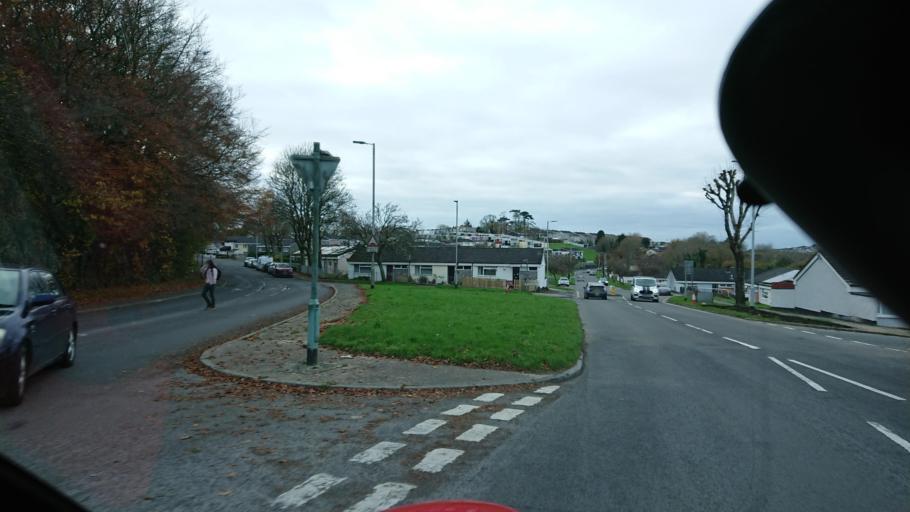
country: GB
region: England
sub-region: Plymouth
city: Plymouth
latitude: 50.4093
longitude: -4.1474
